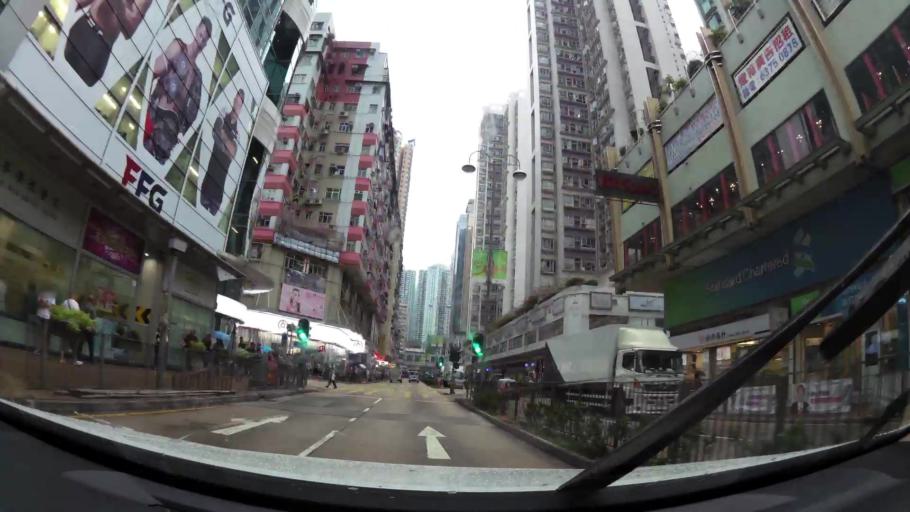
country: HK
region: Tsuen Wan
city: Tsuen Wan
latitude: 22.3696
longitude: 114.1172
